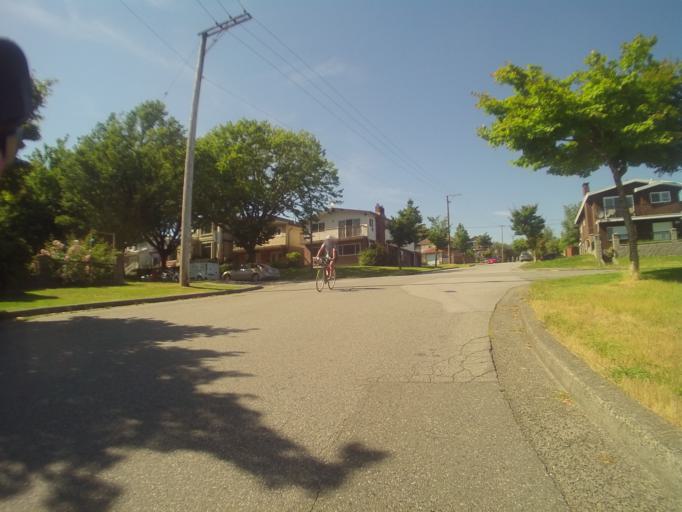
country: CA
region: British Columbia
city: Vancouver
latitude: 49.2136
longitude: -123.0801
